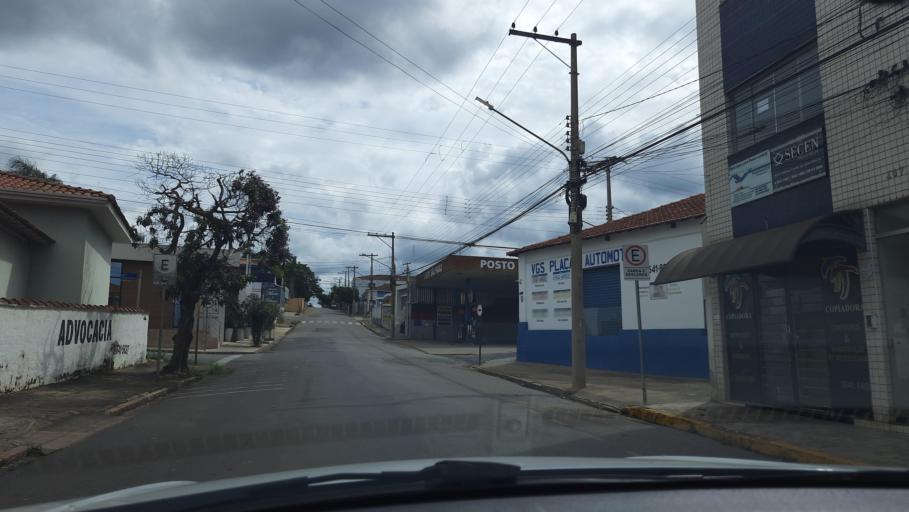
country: BR
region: Sao Paulo
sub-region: Vargem Grande Do Sul
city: Vargem Grande do Sul
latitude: -21.8357
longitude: -46.8975
